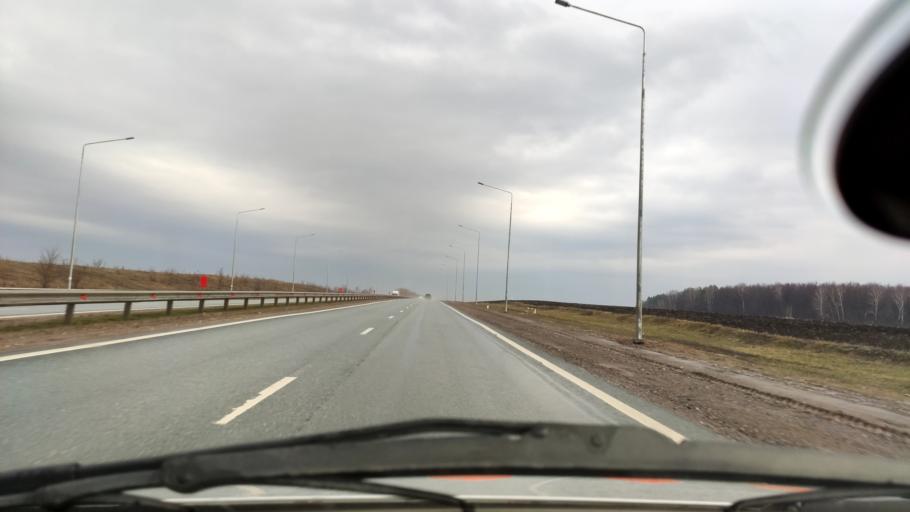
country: RU
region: Bashkortostan
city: Tolbazy
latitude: 53.8289
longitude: 55.9251
